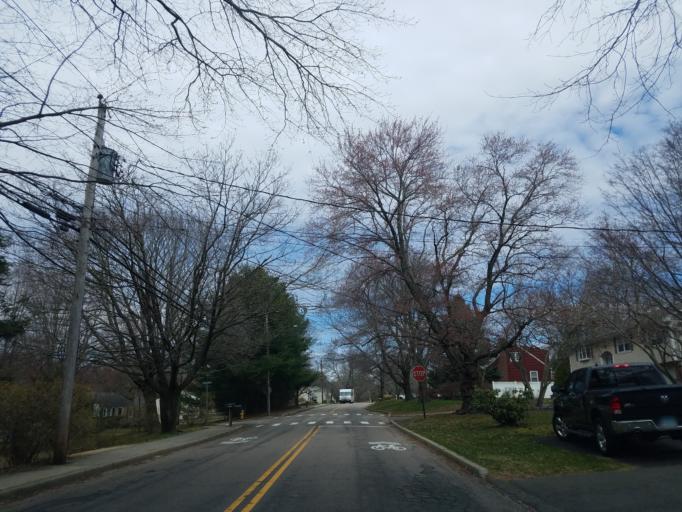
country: US
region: Connecticut
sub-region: Fairfield County
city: Bridgeport
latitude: 41.1856
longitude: -73.2437
